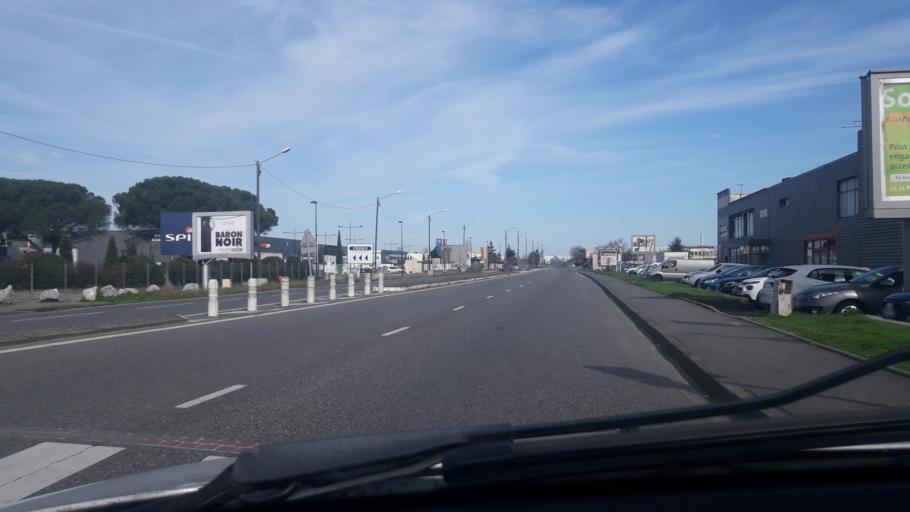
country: FR
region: Midi-Pyrenees
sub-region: Departement de la Haute-Garonne
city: Portet-sur-Garonne
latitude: 43.5493
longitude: 1.4205
